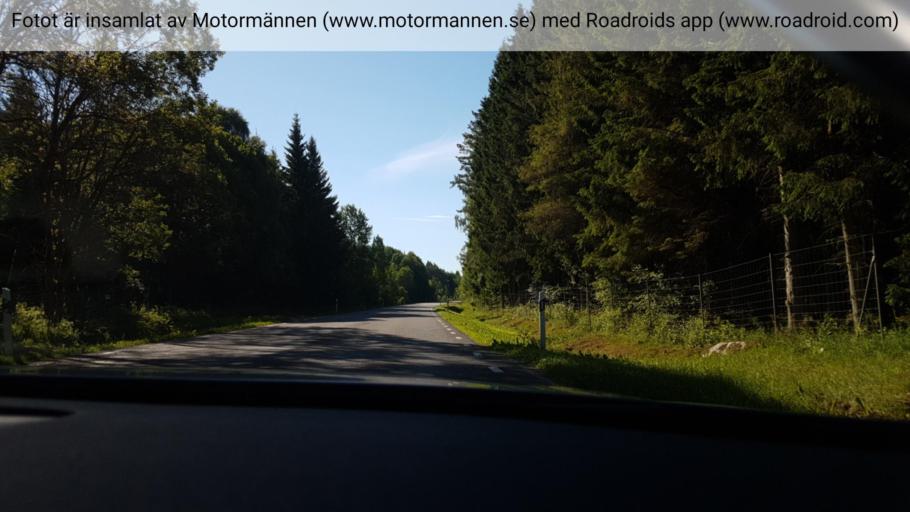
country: SE
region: Vaestra Goetaland
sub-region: Falkopings Kommun
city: Falkoeping
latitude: 58.0614
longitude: 13.5376
